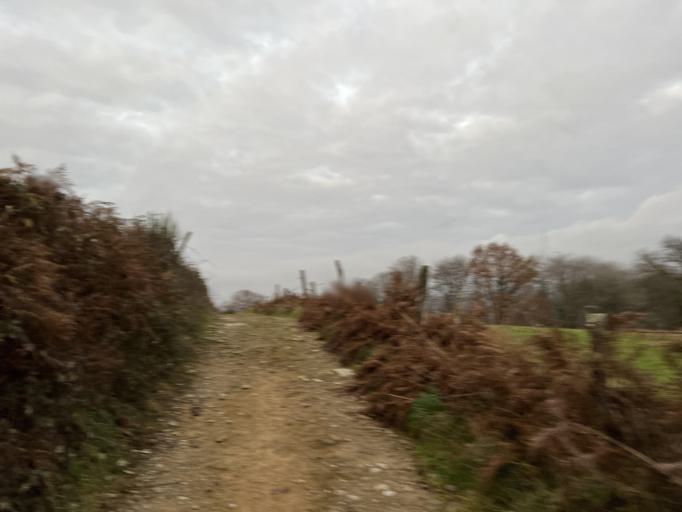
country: FR
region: Limousin
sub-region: Departement de la Correze
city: Sainte-Fortunade
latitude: 45.2207
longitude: 1.7791
